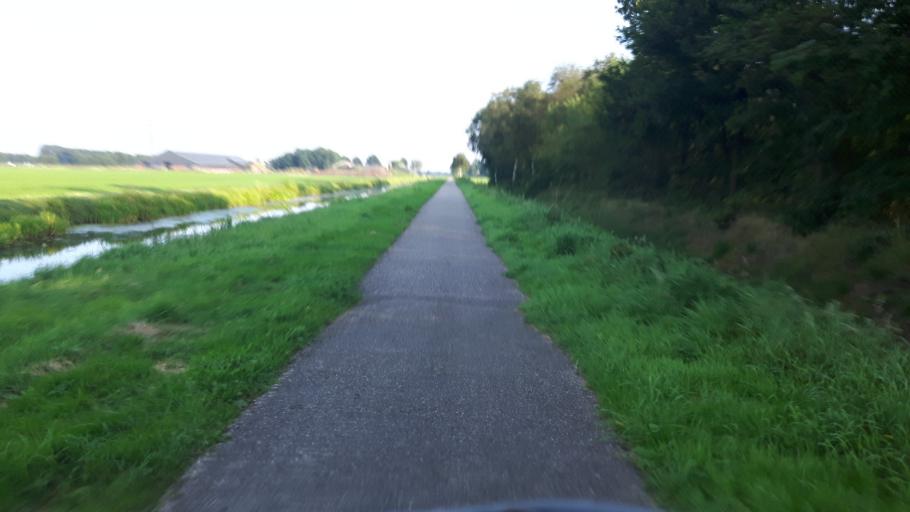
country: NL
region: Drenthe
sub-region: Gemeente Tynaarlo
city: Vries
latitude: 53.1207
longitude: 6.5008
